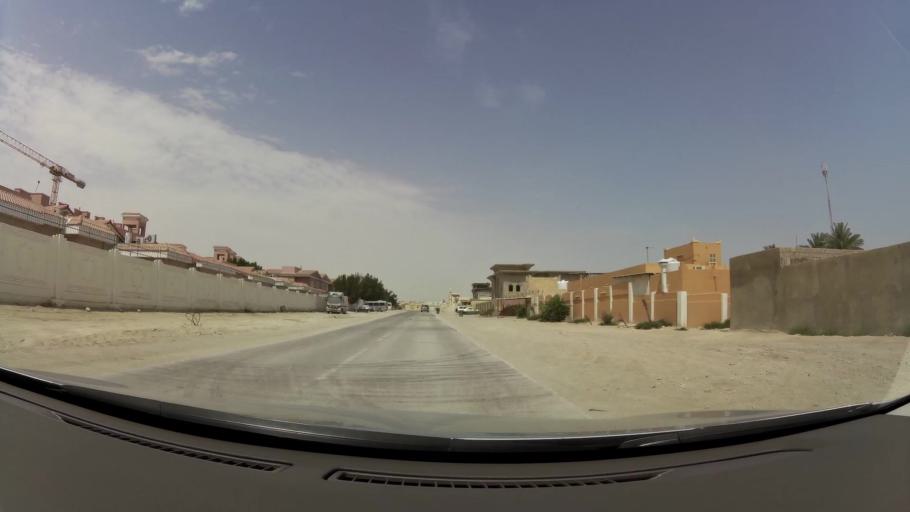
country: QA
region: Baladiyat ar Rayyan
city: Ar Rayyan
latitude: 25.3499
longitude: 51.4702
